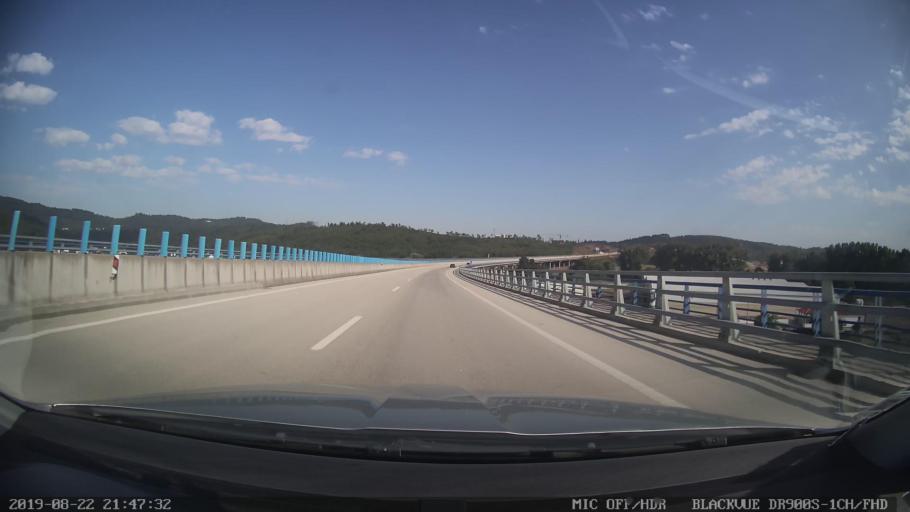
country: PT
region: Coimbra
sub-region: Penela
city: Penela
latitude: 40.0078
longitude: -8.3662
